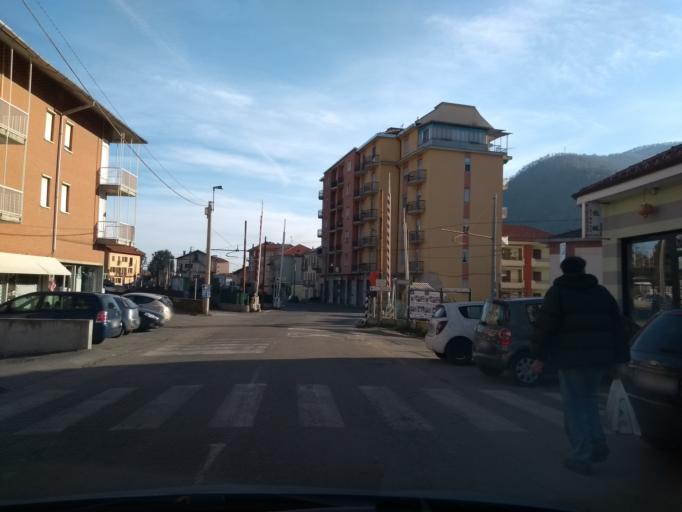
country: IT
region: Piedmont
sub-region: Provincia di Torino
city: Lanzo Torinese
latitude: 45.2735
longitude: 7.4823
